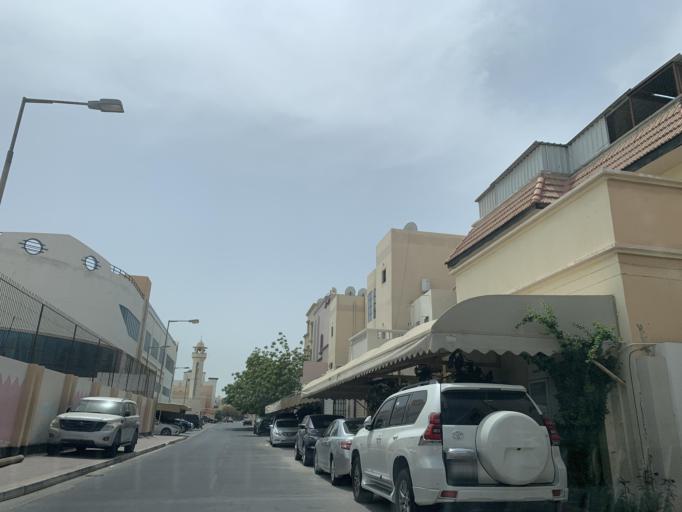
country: BH
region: Northern
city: Ar Rifa'
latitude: 26.1342
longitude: 50.5637
